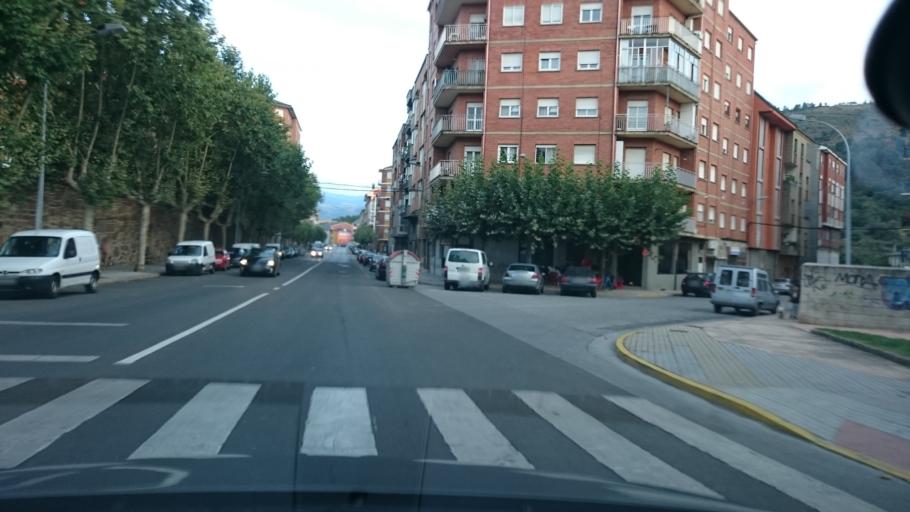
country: ES
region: Castille and Leon
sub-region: Provincia de Leon
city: Ponferrada
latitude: 42.5449
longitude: -6.6025
